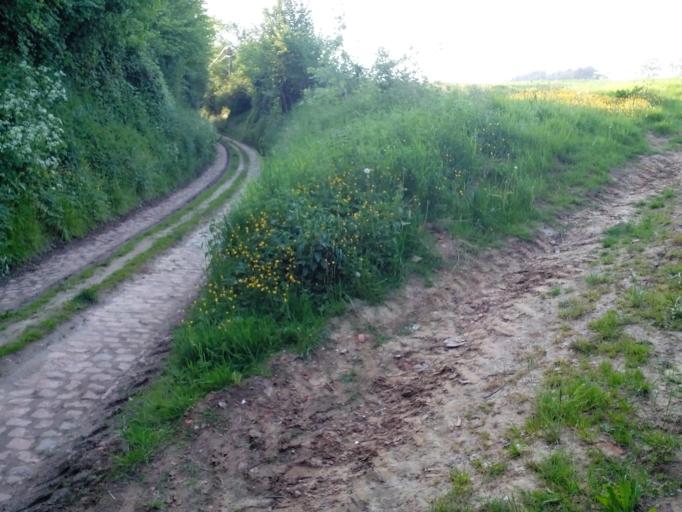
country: BE
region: Flanders
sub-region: Provincie Vlaams-Brabant
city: Bertem
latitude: 50.8666
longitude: 4.6251
